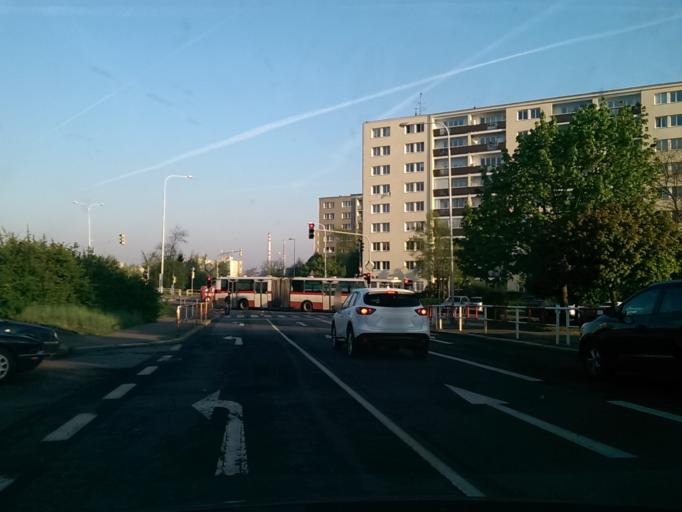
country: CZ
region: Praha
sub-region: Praha 8
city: Karlin
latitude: 50.0465
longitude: 14.4867
